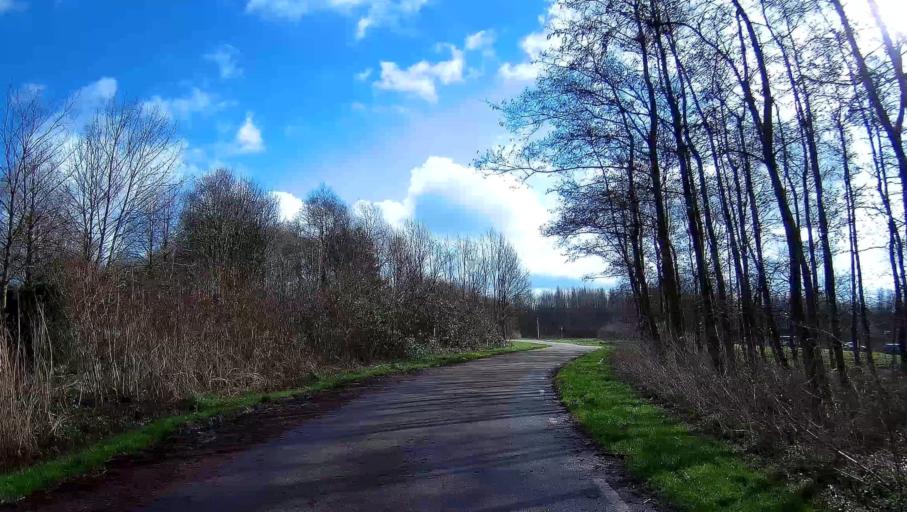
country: NL
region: South Holland
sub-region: Gemeente Pijnacker-Nootdorp
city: Pijnacker
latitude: 52.0360
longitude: 4.4050
